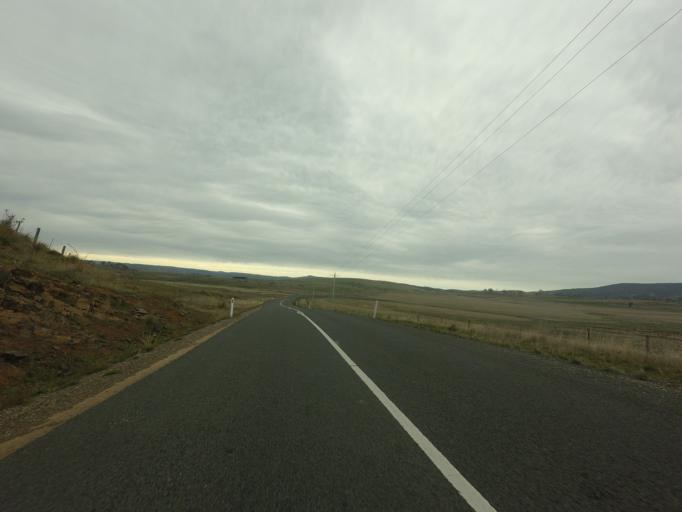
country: AU
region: Tasmania
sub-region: Derwent Valley
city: New Norfolk
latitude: -42.4322
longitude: 146.9859
